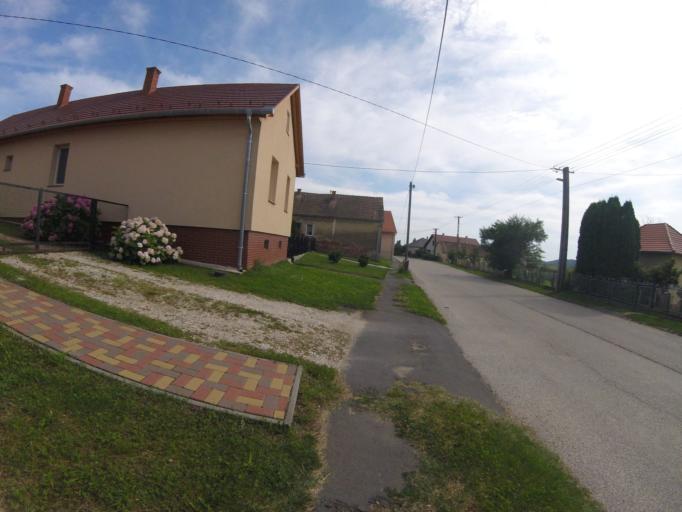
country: HR
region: Medimurska
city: Podturen
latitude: 46.5408
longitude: 16.5927
